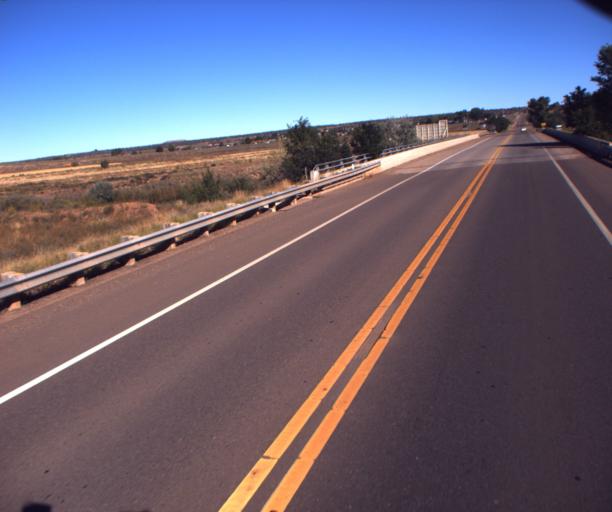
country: US
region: Arizona
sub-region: Navajo County
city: Snowflake
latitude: 34.5214
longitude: -110.0795
